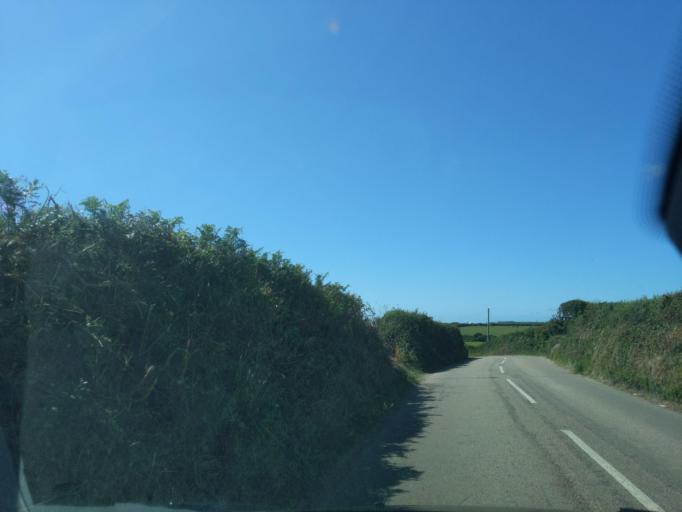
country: GB
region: England
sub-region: Cornwall
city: St. Buryan
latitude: 50.0540
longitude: -5.6533
